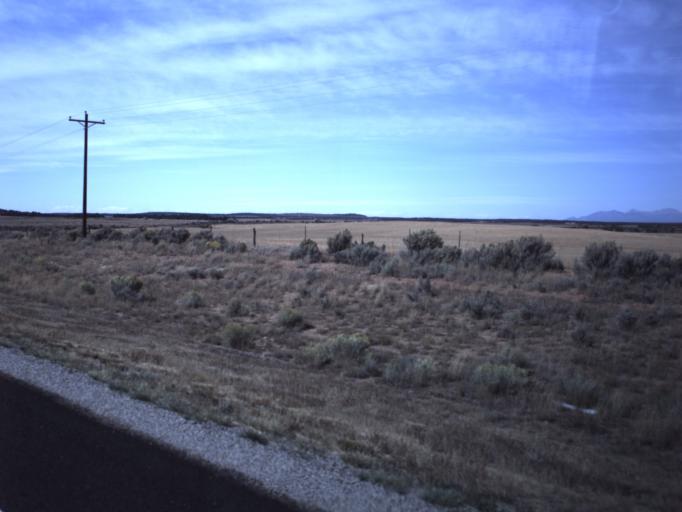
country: US
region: Colorado
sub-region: Dolores County
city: Dove Creek
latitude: 37.8192
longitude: -109.0515
